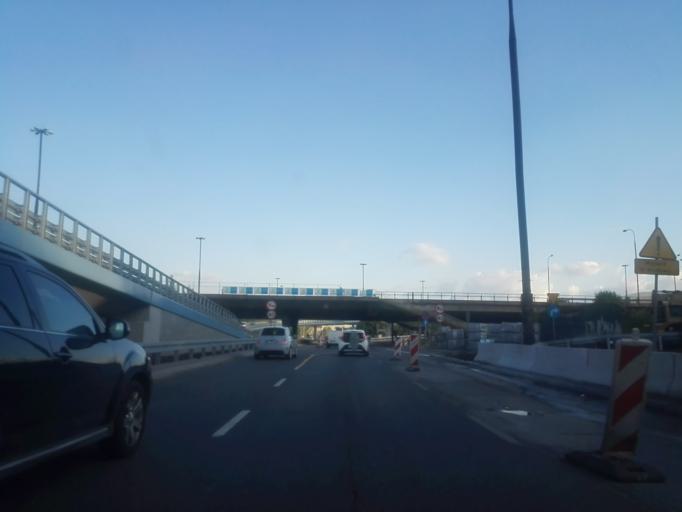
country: PL
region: Masovian Voivodeship
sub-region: Warszawa
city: Srodmiescie
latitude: 52.2252
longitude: 21.0433
